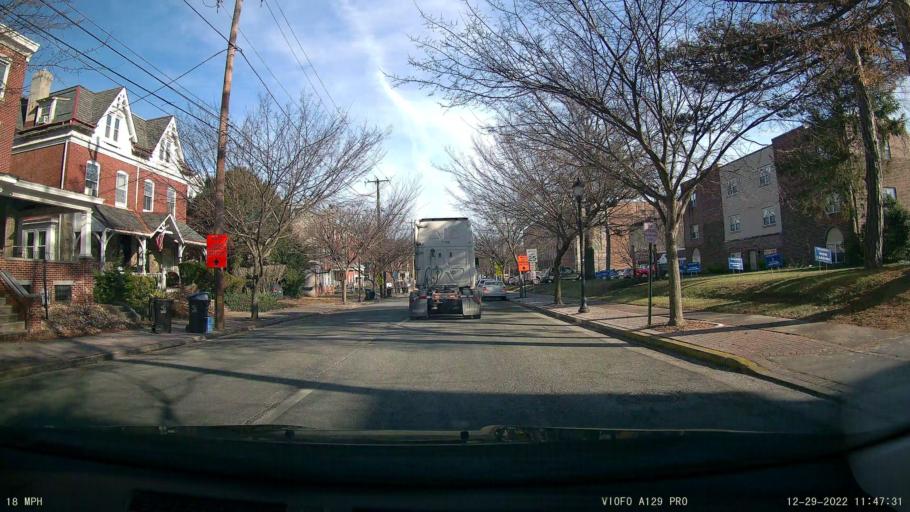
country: US
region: Pennsylvania
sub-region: Montgomery County
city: Norristown
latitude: 40.1225
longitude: -75.3346
